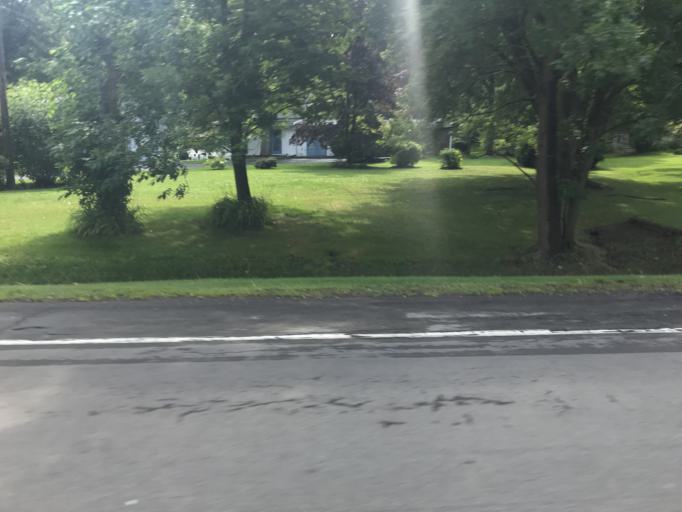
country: US
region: New York
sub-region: Chautauqua County
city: Dunkirk
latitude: 42.5174
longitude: -79.2713
